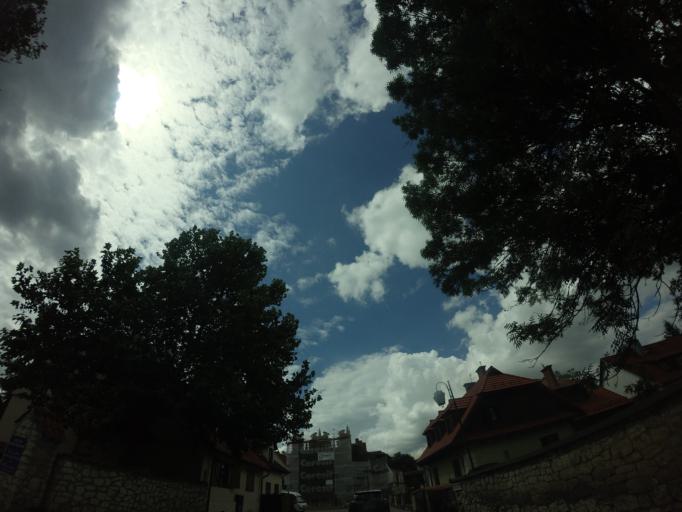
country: PL
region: Lublin Voivodeship
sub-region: Powiat pulawski
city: Kazimierz Dolny
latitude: 51.3225
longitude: 21.9462
